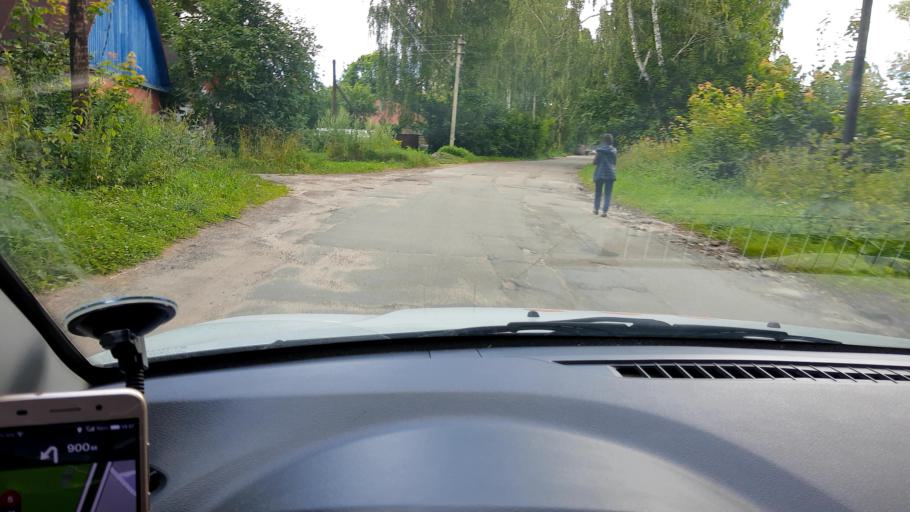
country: RU
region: Nizjnij Novgorod
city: Afonino
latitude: 56.2048
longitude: 44.0231
